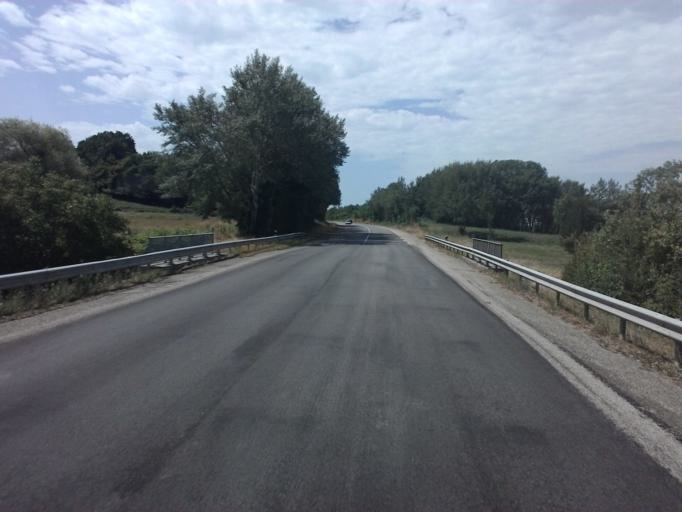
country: FR
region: Franche-Comte
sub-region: Departement du Jura
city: Cousance
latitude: 46.5250
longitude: 5.3923
